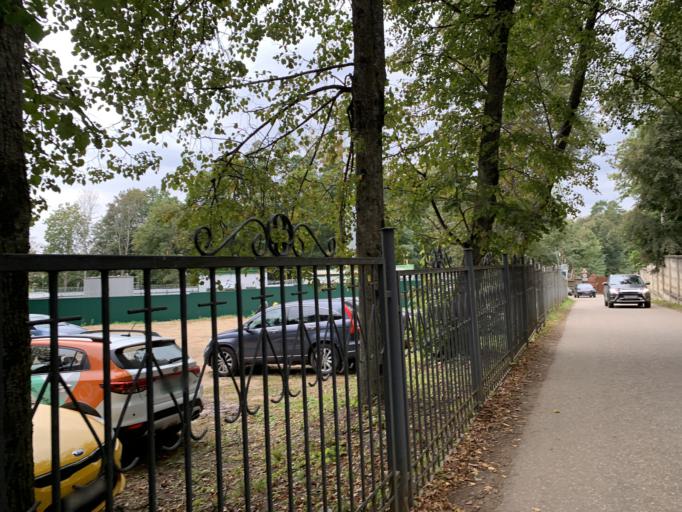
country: RU
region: Moskovskaya
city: Zvenigorod
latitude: 55.7311
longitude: 36.8154
